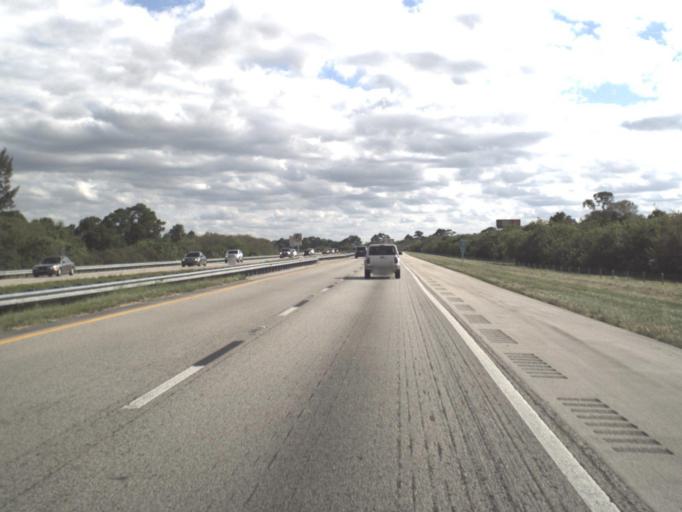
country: US
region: Florida
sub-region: Saint Lucie County
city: Lakewood Park
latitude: 27.4470
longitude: -80.4273
